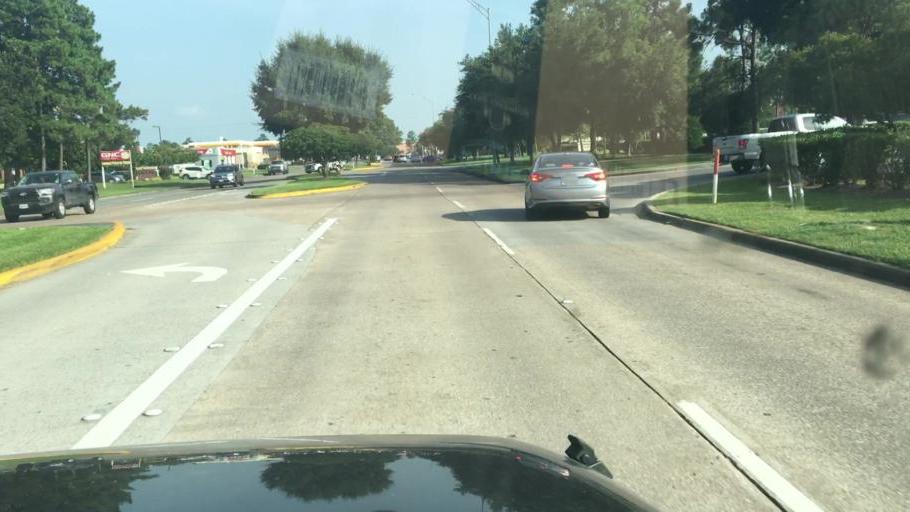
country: US
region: Texas
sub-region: Harris County
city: Atascocita
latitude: 30.0010
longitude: -95.1633
